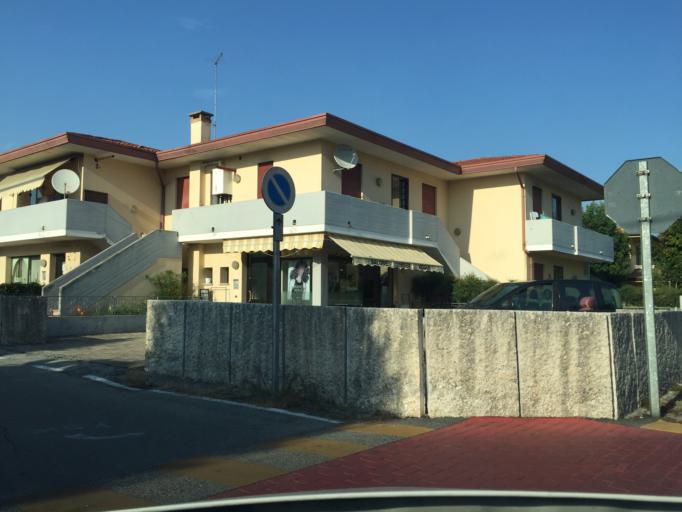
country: IT
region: Veneto
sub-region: Provincia di Padova
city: Cittadella
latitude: 45.6383
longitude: 11.7824
